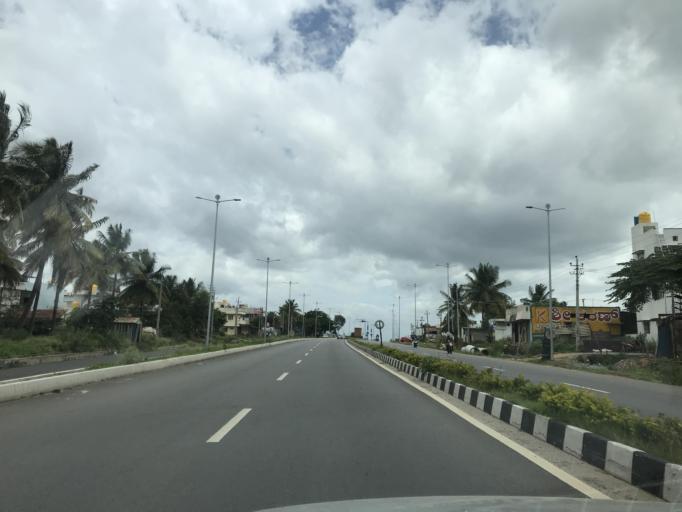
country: IN
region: Karnataka
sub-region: Tumkur
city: Tumkur
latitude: 13.3085
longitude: 77.1449
